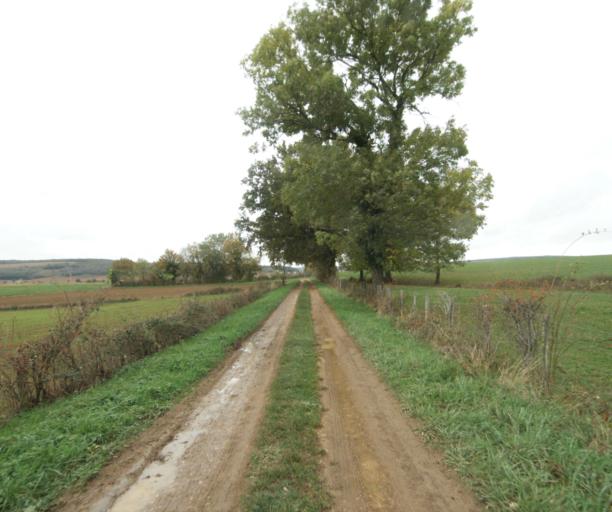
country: FR
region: Rhone-Alpes
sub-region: Departement de l'Ain
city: Pont-de-Vaux
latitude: 46.4623
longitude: 4.8707
